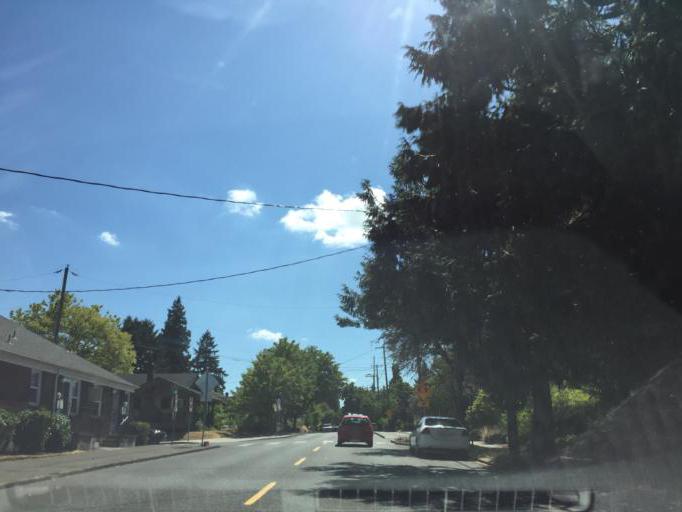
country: US
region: Oregon
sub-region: Multnomah County
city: Portland
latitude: 45.5572
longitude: -122.6307
